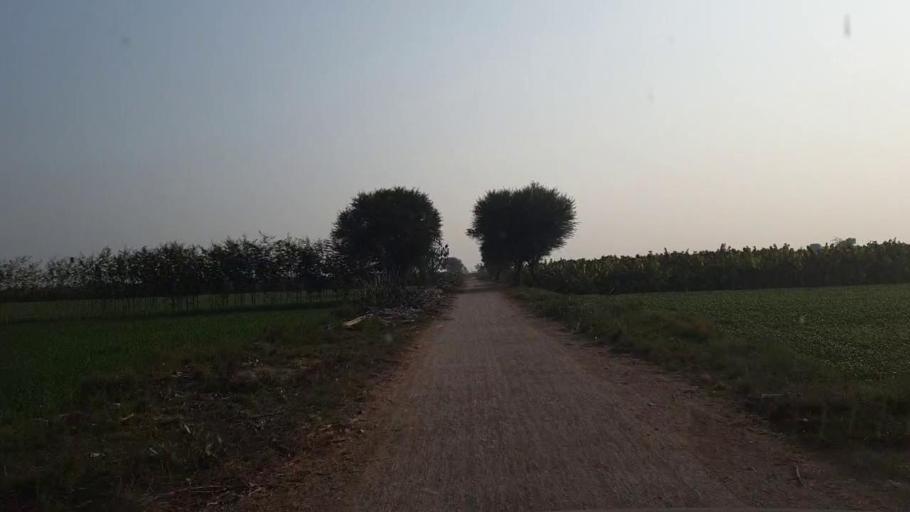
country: PK
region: Sindh
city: Hala
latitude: 25.8941
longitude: 68.4498
